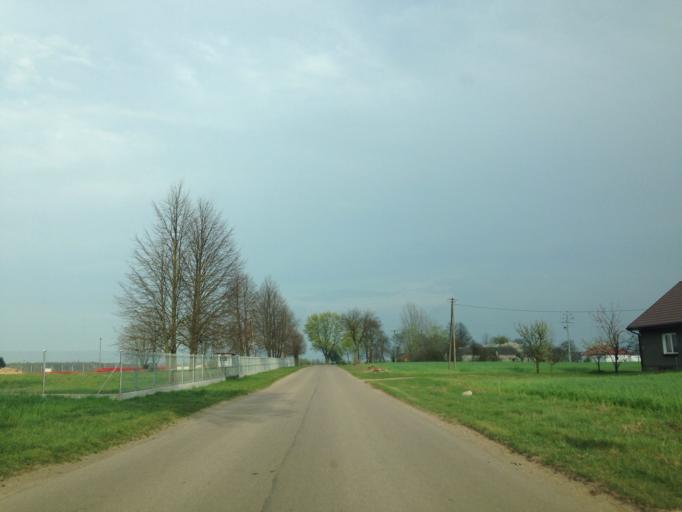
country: PL
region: Masovian Voivodeship
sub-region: Powiat zurominski
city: Siemiatkowo
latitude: 52.9643
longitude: 20.0083
